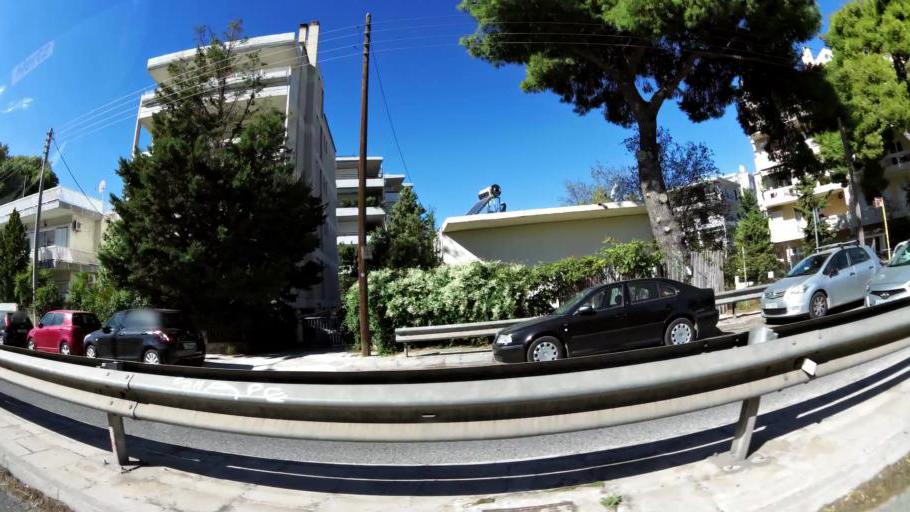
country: GR
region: Attica
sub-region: Nomarchia Athinas
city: Khalandrion
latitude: 38.0339
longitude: 23.8049
